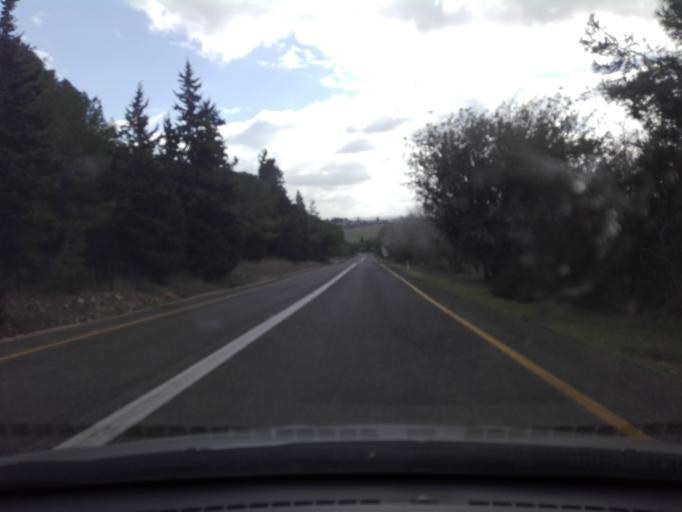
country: IL
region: Haifa
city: Daliyat el Karmil
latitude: 32.6436
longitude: 35.0573
